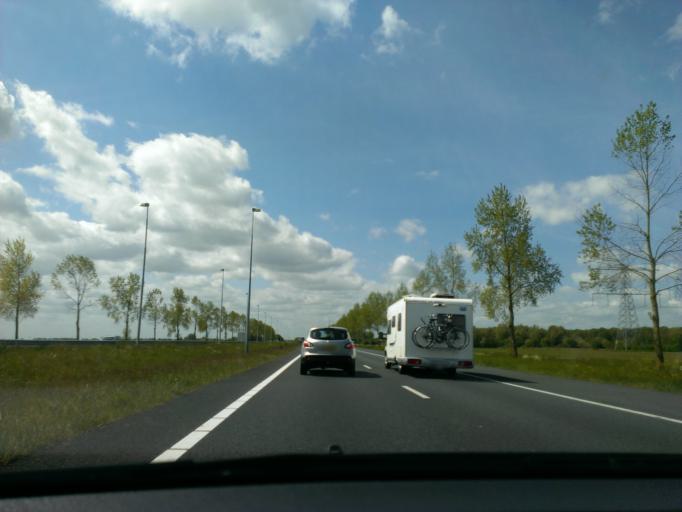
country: NL
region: Flevoland
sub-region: Gemeente Lelystad
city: Lelystad
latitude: 52.4699
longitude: 5.4812
